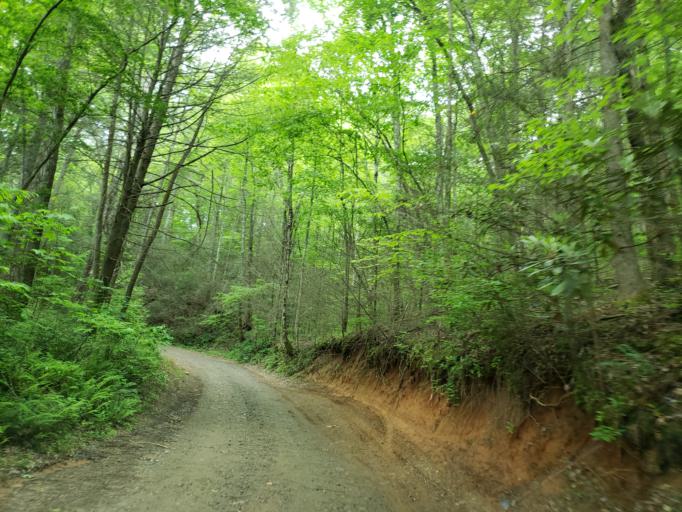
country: US
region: Georgia
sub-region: Fannin County
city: Blue Ridge
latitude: 34.8431
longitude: -84.4435
